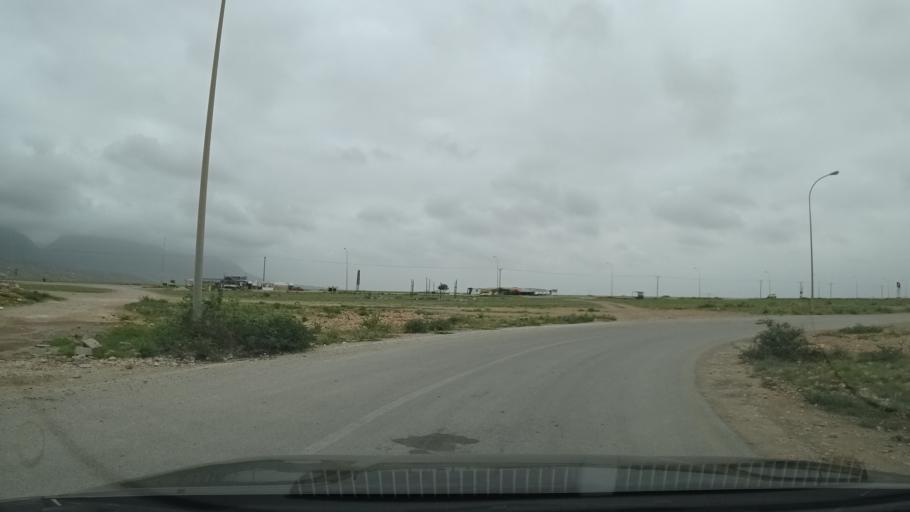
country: OM
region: Zufar
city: Salalah
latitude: 17.1000
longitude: 54.2156
